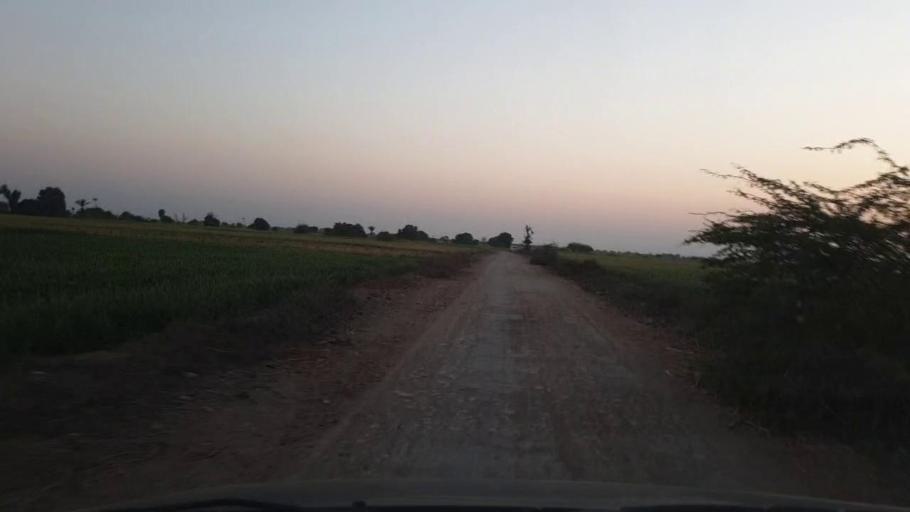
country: PK
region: Sindh
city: Digri
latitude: 25.1890
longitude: 69.1883
